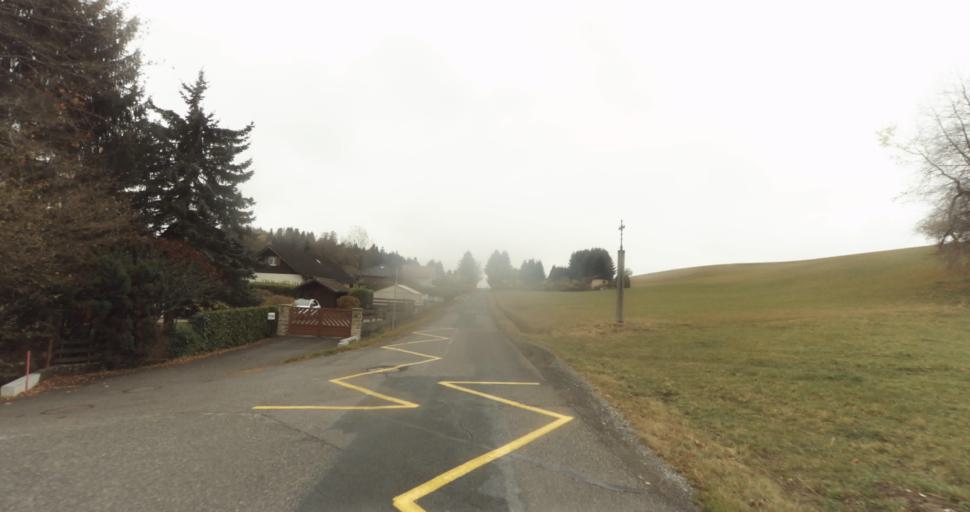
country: FR
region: Rhone-Alpes
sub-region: Departement de la Haute-Savoie
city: Evires
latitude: 46.0399
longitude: 6.2306
